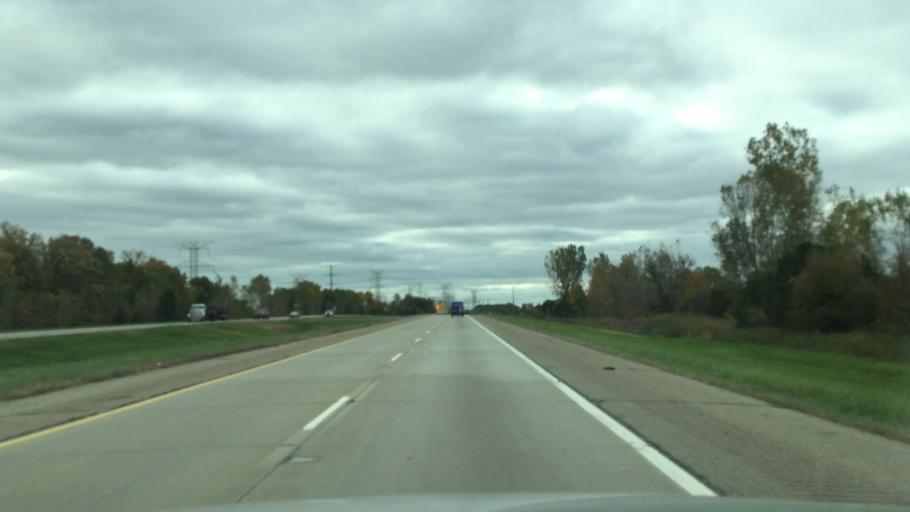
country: US
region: Michigan
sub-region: Macomb County
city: Romeo
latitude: 42.7675
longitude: -83.0093
